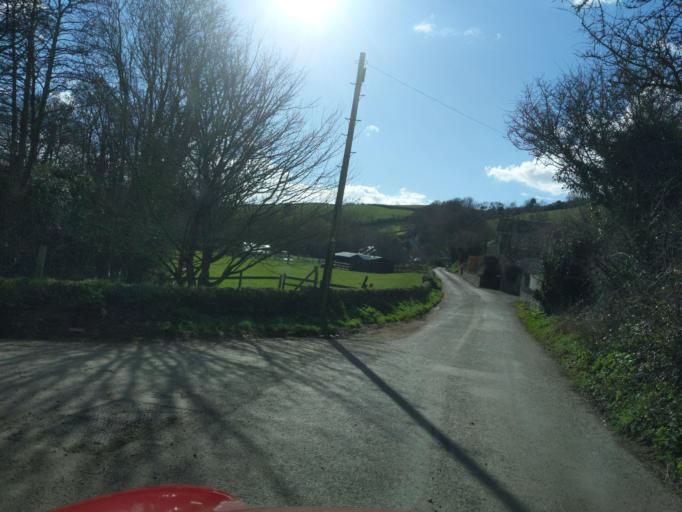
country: GB
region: England
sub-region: Devon
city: Kingsbridge
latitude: 50.2863
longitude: -3.7555
